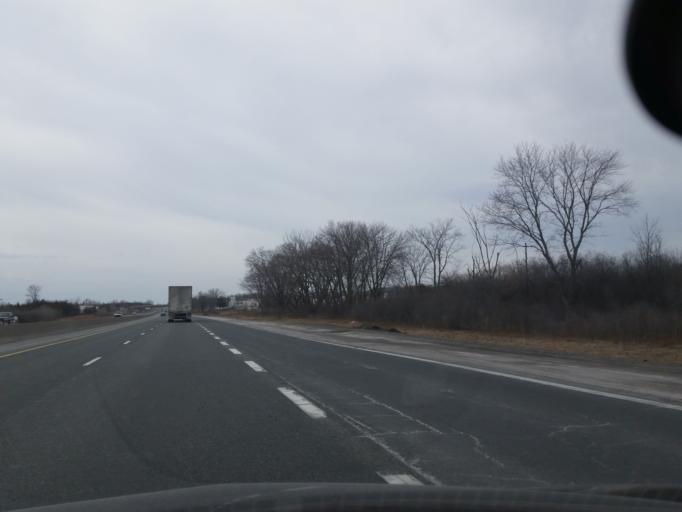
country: CA
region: Ontario
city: Belleville
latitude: 44.1915
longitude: -77.4013
